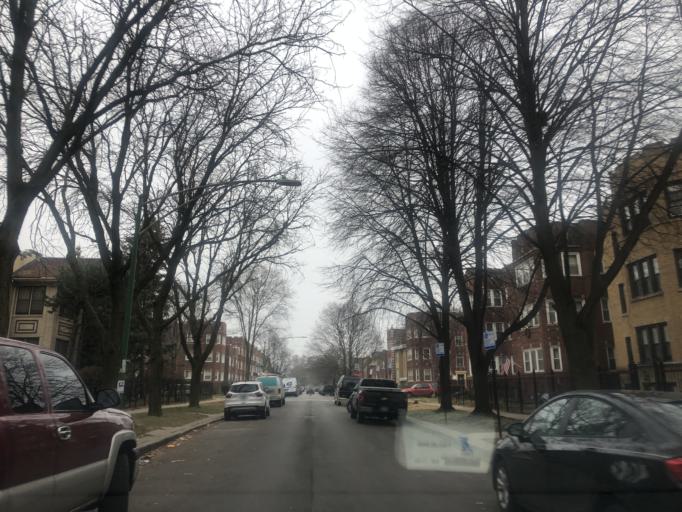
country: US
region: Illinois
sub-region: Cook County
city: Evergreen Park
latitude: 41.7501
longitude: -87.6113
